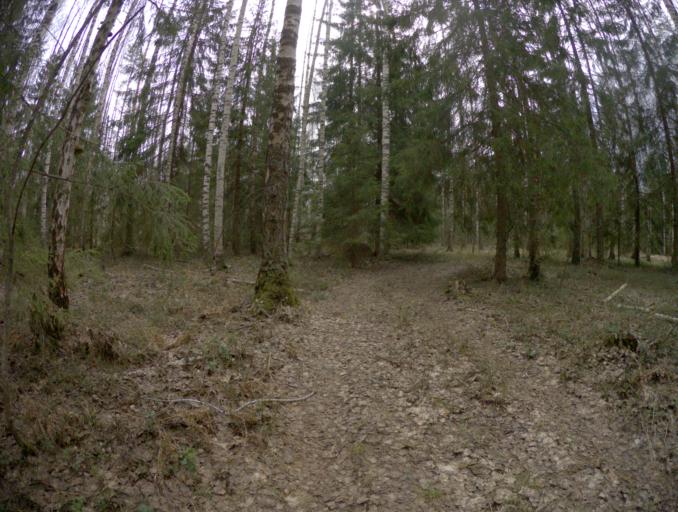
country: RU
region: Vladimir
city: Raduzhnyy
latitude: 55.9389
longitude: 40.2637
